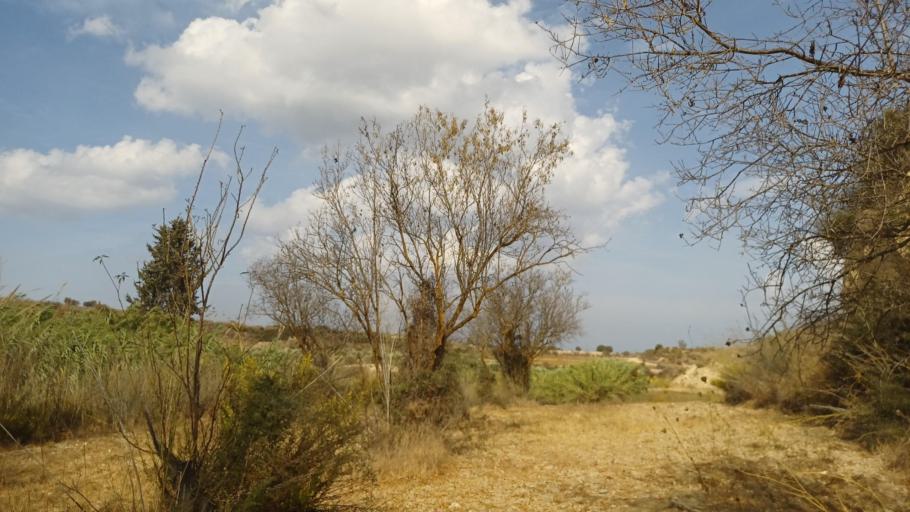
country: CY
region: Pafos
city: Polis
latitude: 35.0131
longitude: 32.4155
